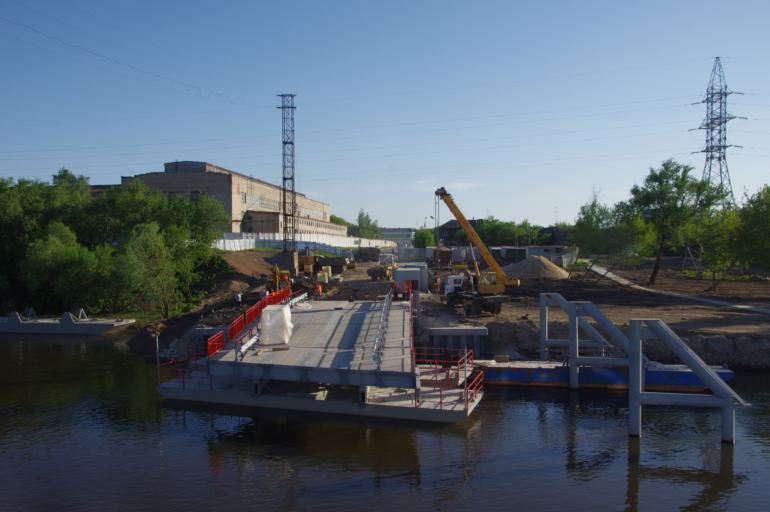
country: RU
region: Moskovskaya
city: Kolomna
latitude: 55.0964
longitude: 38.7990
